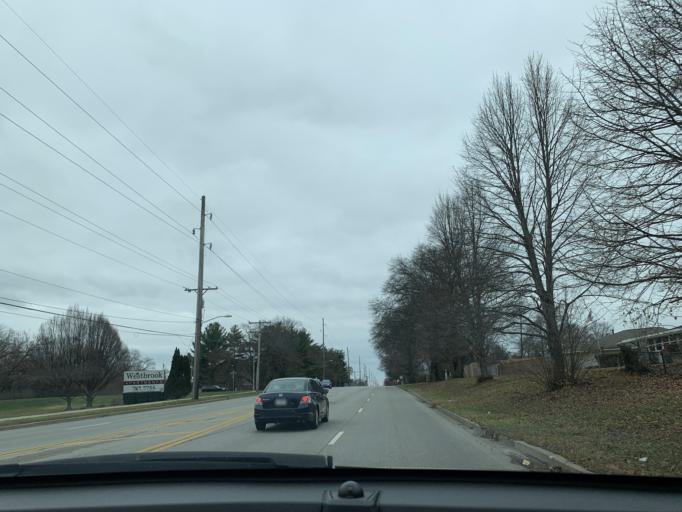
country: US
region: Illinois
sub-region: Sangamon County
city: Jerome
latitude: 39.7605
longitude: -89.6869
